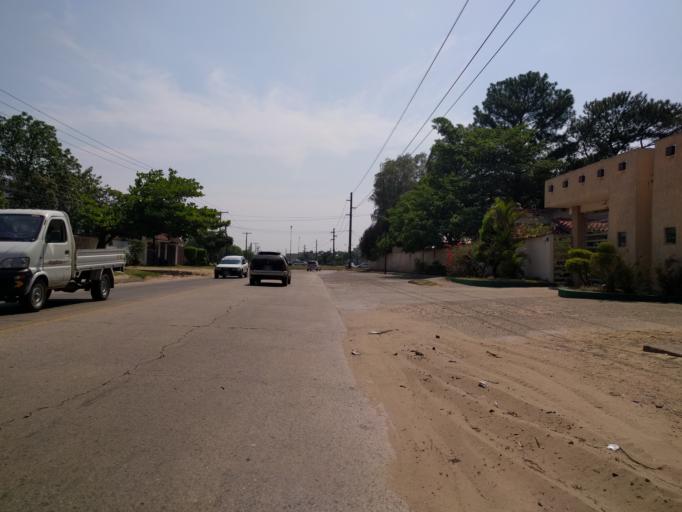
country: BO
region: Santa Cruz
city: Santa Cruz de la Sierra
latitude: -17.8016
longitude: -63.1618
